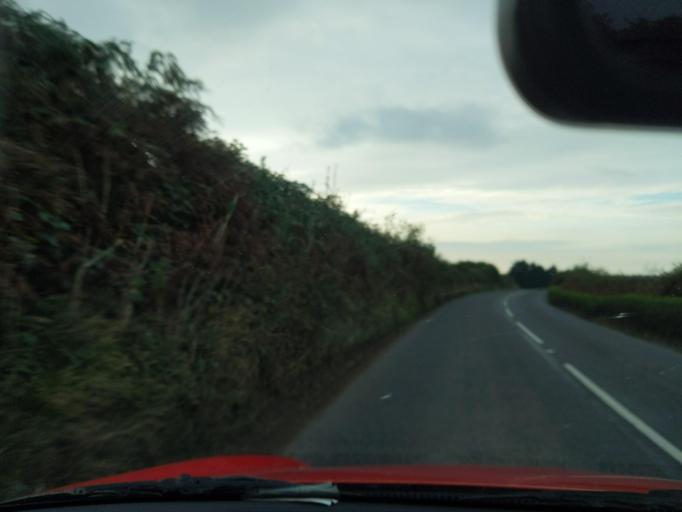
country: GB
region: England
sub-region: Devon
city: Great Torrington
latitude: 50.9121
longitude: -4.1341
